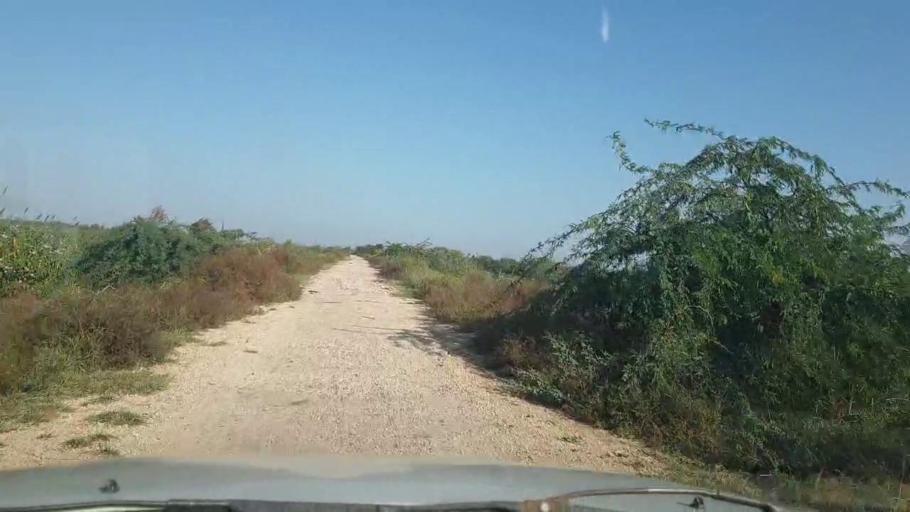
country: PK
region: Sindh
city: Chuhar Jamali
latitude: 24.5525
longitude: 67.9089
